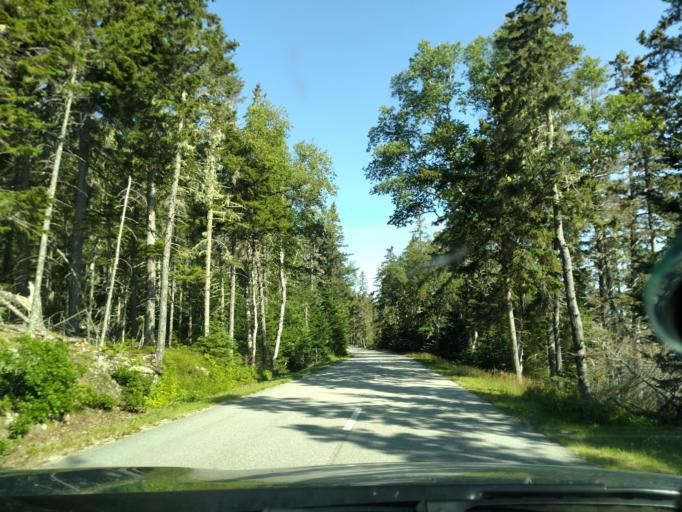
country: US
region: Maine
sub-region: Hancock County
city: Gouldsboro
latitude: 44.3440
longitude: -68.0446
